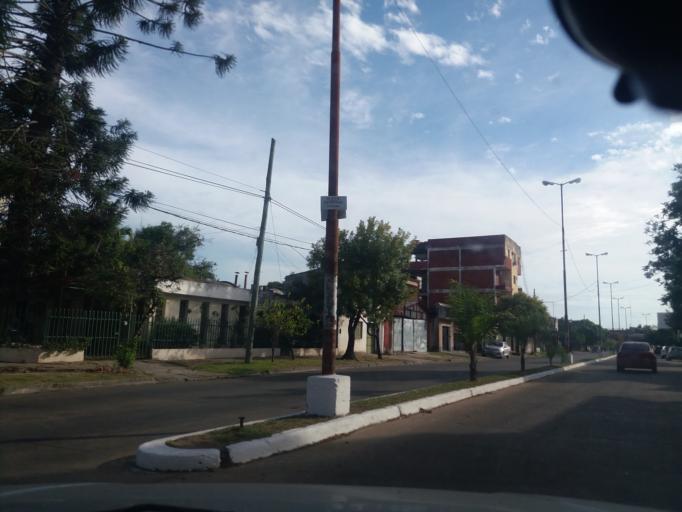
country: AR
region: Corrientes
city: Corrientes
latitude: -27.4852
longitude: -58.8326
